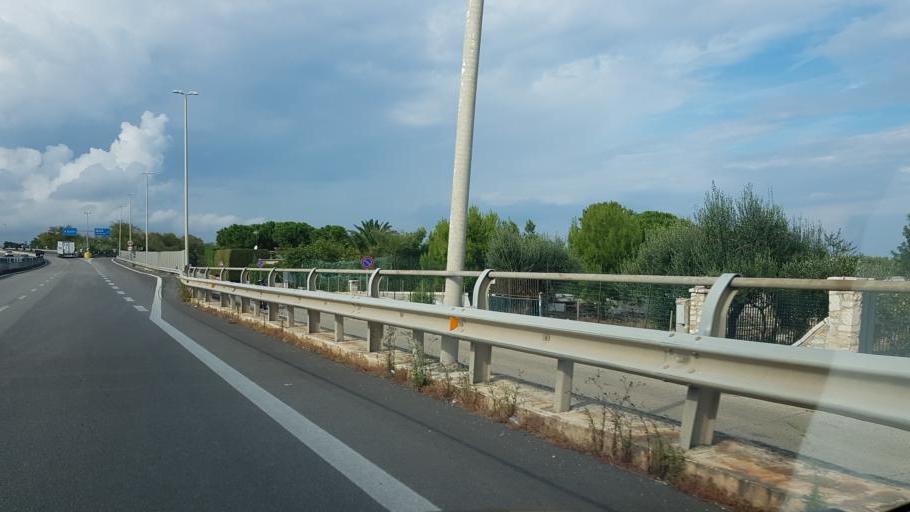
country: IT
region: Apulia
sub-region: Provincia di Bari
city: Mola di Bari
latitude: 41.0319
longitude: 17.1464
